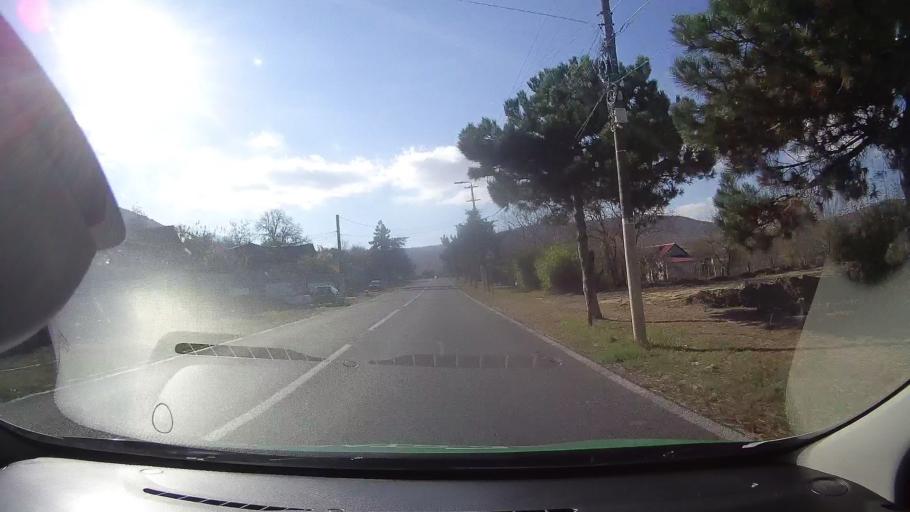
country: RO
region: Tulcea
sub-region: Oras Babadag
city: Babadag
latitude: 44.8804
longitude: 28.6932
